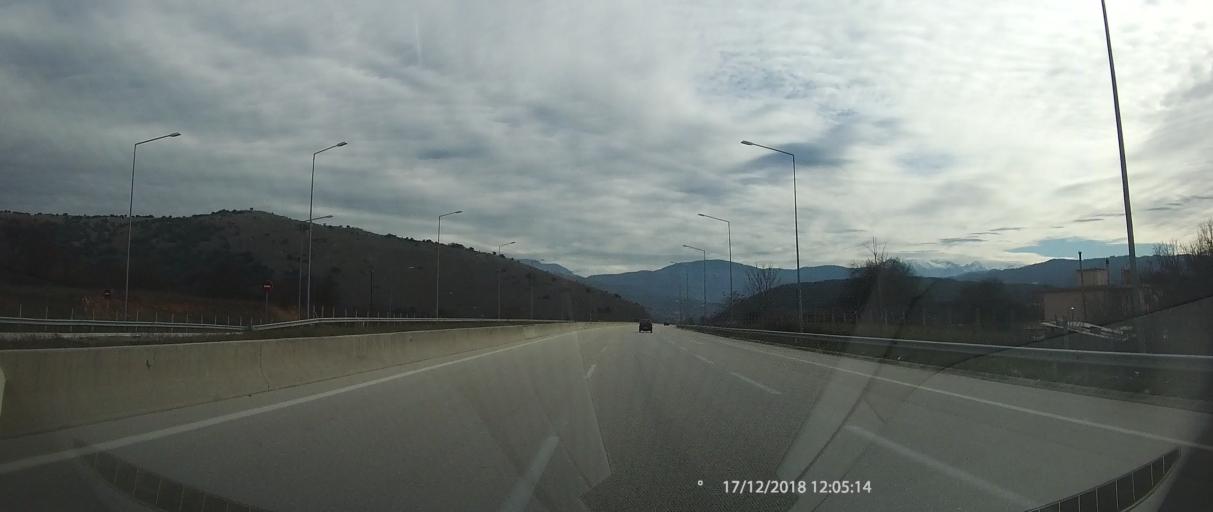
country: GR
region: Epirus
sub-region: Nomos Ioanninon
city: Koutselio
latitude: 39.6003
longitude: 20.9058
